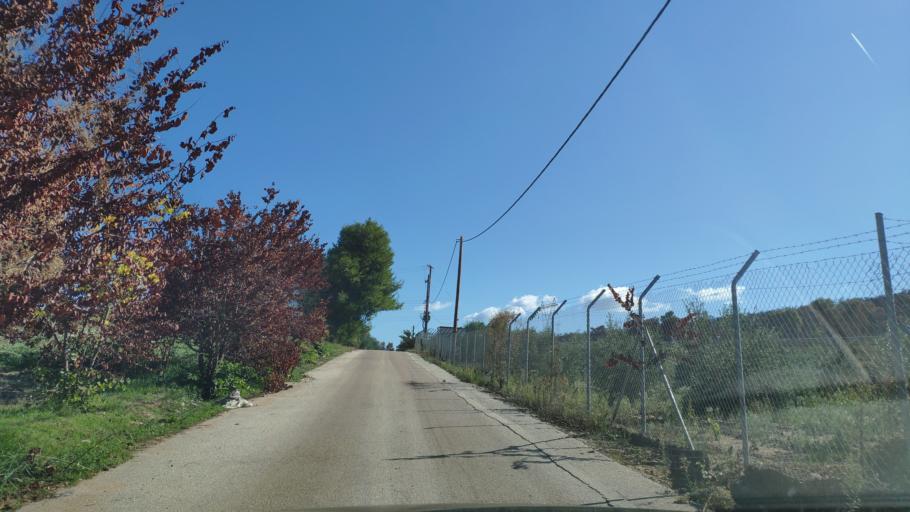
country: GR
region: Peloponnese
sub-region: Nomos Korinthias
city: Athikia
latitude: 37.8447
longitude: 22.9383
